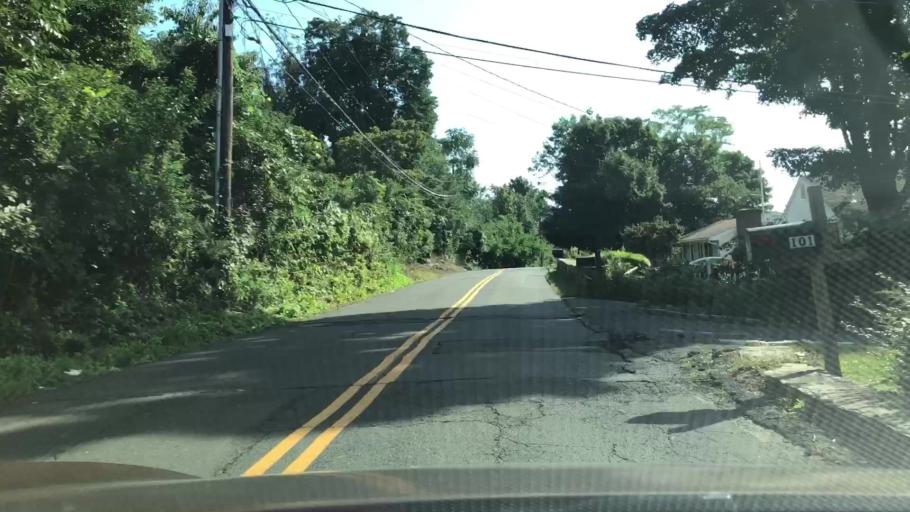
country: US
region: Connecticut
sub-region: Fairfield County
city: Darien
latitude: 41.0990
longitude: -73.4467
